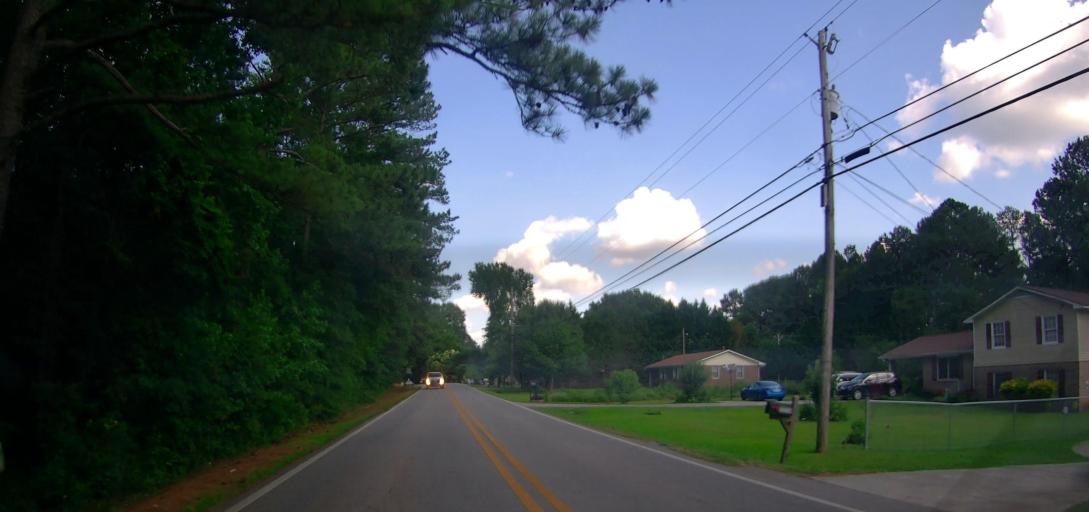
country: US
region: Georgia
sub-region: Spalding County
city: East Griffin
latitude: 33.2819
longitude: -84.2400
